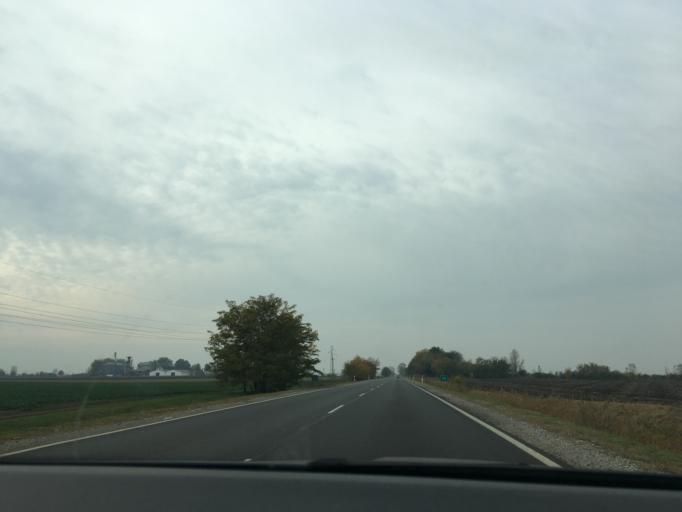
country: HU
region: Hajdu-Bihar
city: Barand
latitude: 47.3467
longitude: 21.1914
